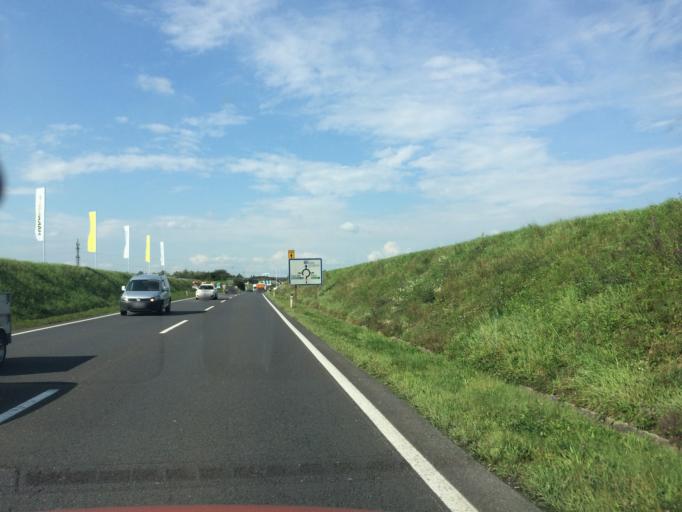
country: AT
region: Upper Austria
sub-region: Politischer Bezirk Linz-Land
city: Traun
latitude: 48.2210
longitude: 14.2279
